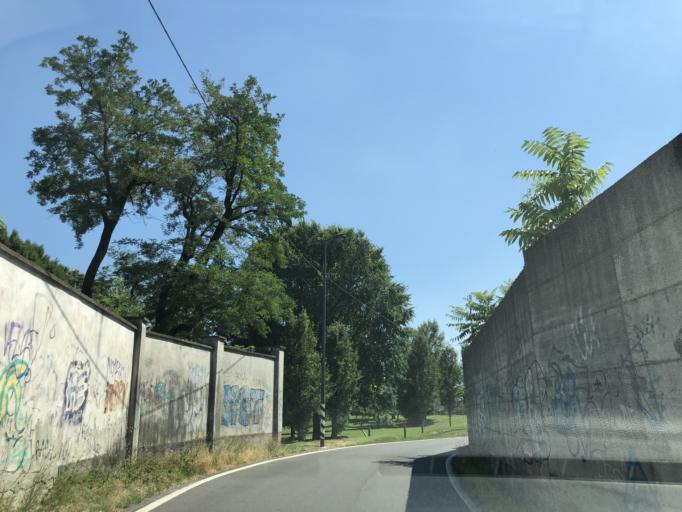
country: IT
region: Lombardy
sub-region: Citta metropolitana di Milano
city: Cormano
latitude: 45.5136
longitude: 9.1673
